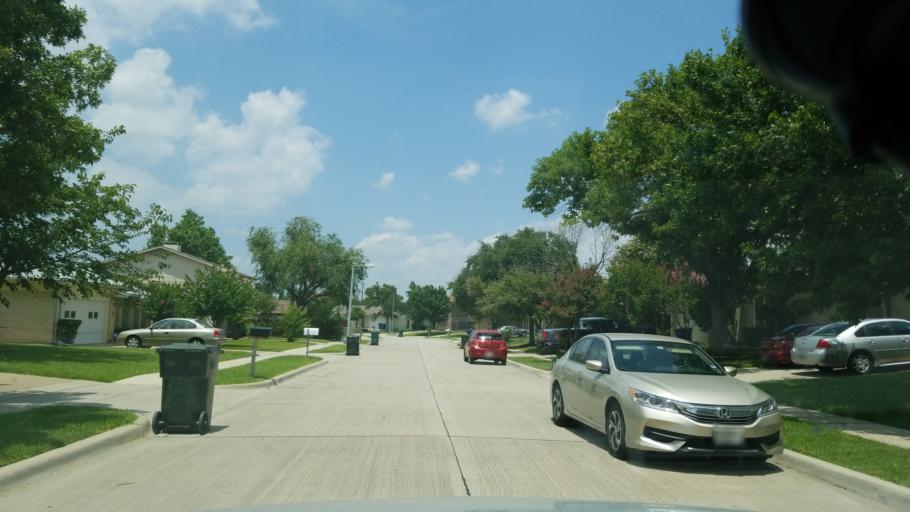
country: US
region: Texas
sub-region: Dallas County
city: Carrollton
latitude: 32.9685
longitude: -96.8688
